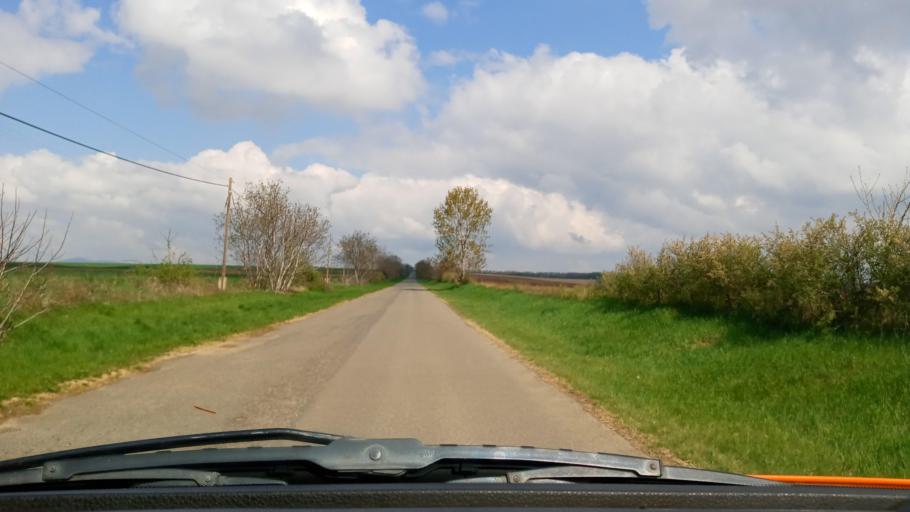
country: HU
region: Baranya
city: Pecsvarad
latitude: 46.0921
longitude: 18.5022
